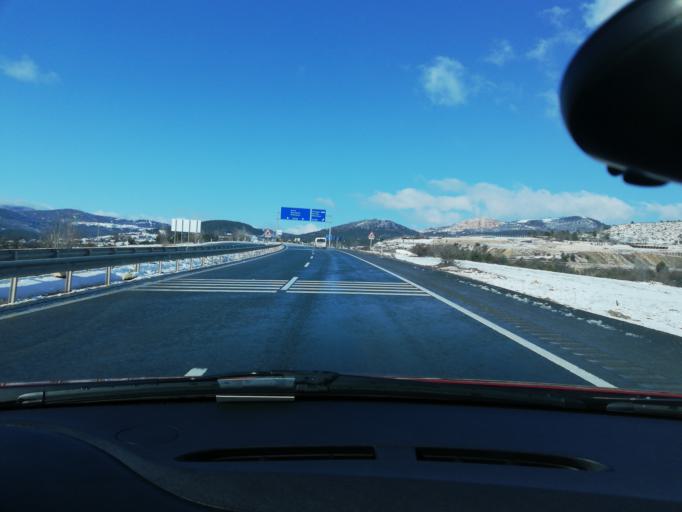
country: TR
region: Kastamonu
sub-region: Cide
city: Kastamonu
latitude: 41.3642
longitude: 33.7295
